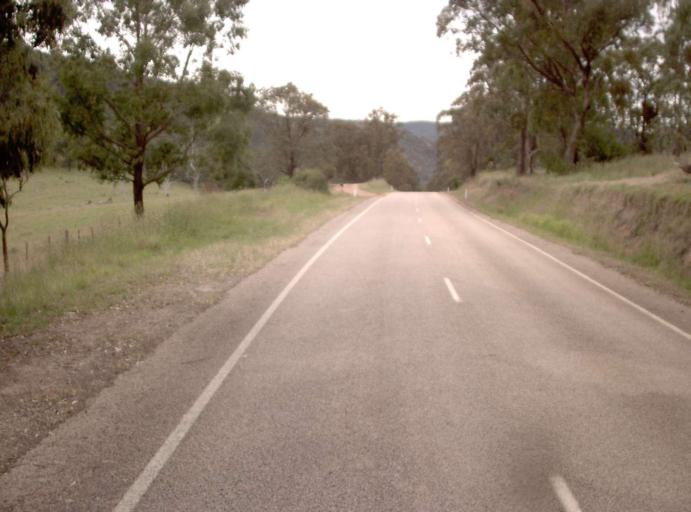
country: AU
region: Victoria
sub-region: East Gippsland
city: Bairnsdale
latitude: -37.5492
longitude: 147.1996
